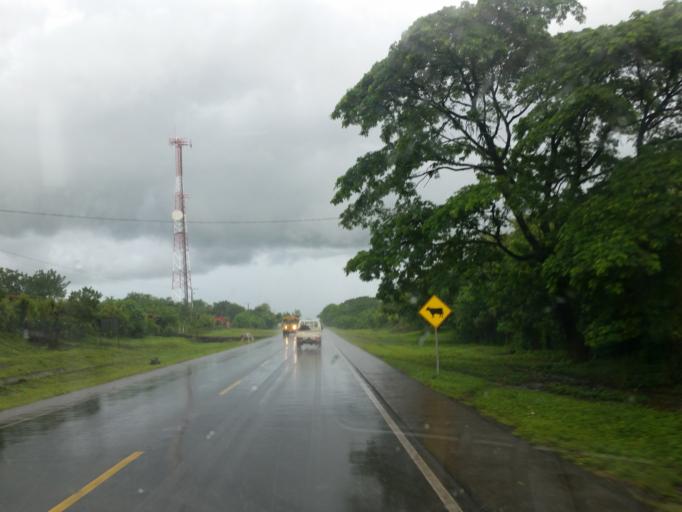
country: NI
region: Chinandega
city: El Viejo
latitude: 12.7166
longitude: -87.0874
